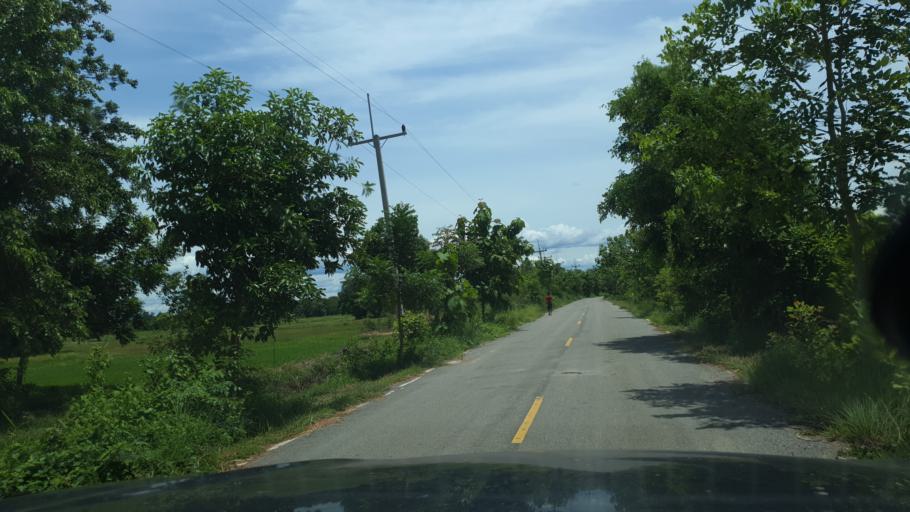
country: TH
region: Sukhothai
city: Ban Na
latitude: 17.1237
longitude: 99.6737
